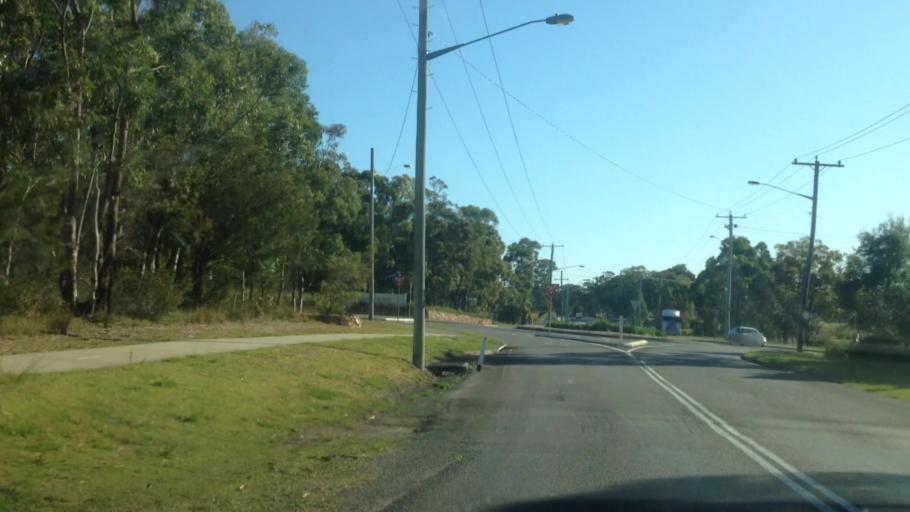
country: AU
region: New South Wales
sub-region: Lake Macquarie Shire
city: Dora Creek
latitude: -33.1087
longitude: 151.5349
